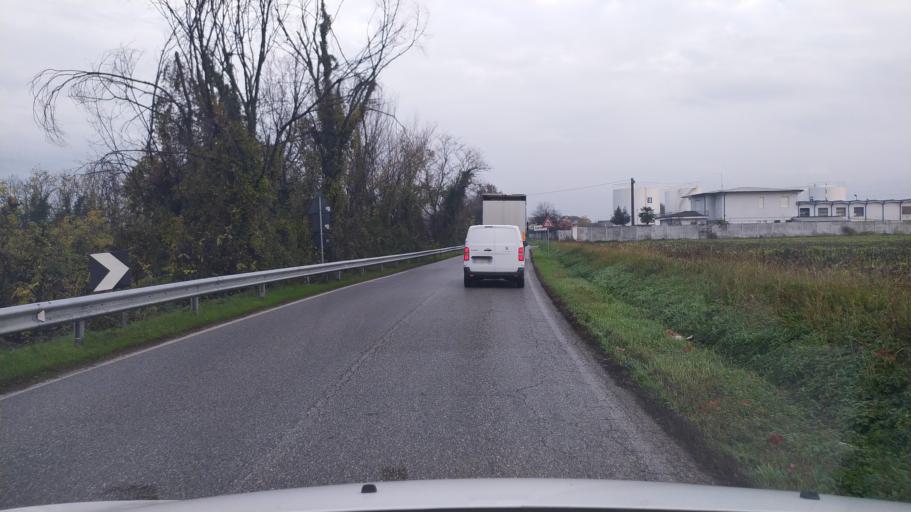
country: IT
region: Lombardy
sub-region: Provincia di Brescia
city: Pontoglio
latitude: 45.5612
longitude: 9.8602
